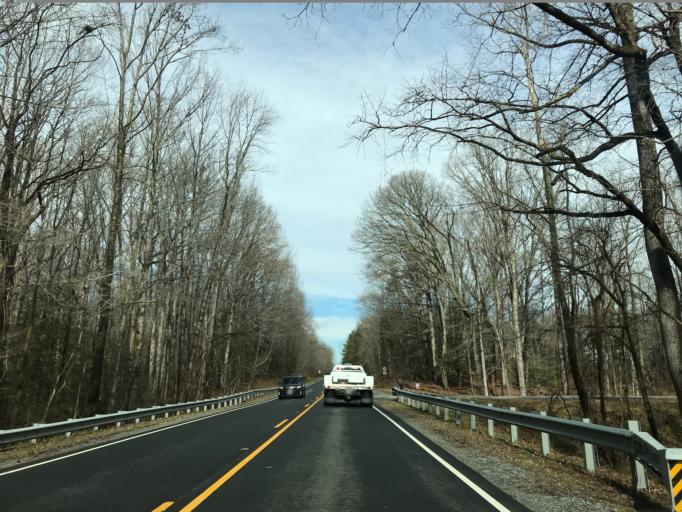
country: US
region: Virginia
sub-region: King George County
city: Dahlgren
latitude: 38.3047
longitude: -77.0750
